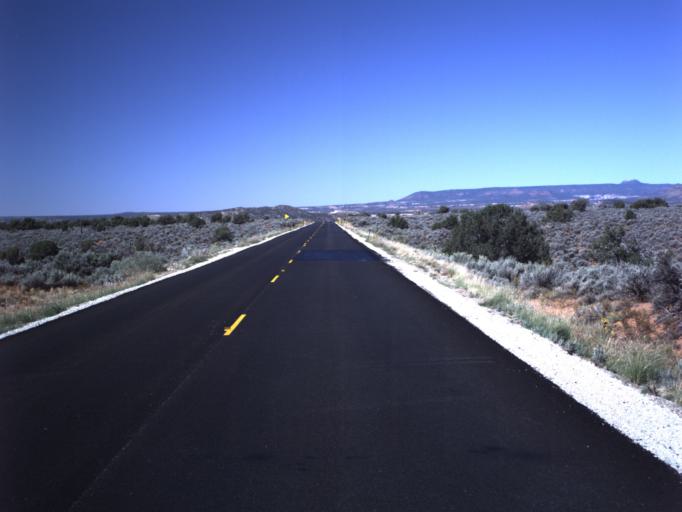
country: US
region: Utah
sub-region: San Juan County
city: Blanding
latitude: 37.5750
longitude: -109.5424
